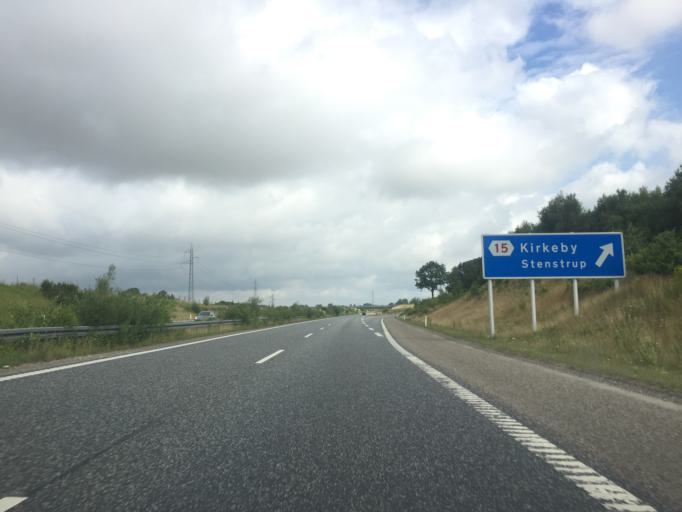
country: DK
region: South Denmark
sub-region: Svendborg Kommune
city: Svendborg
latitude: 55.1088
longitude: 10.5628
